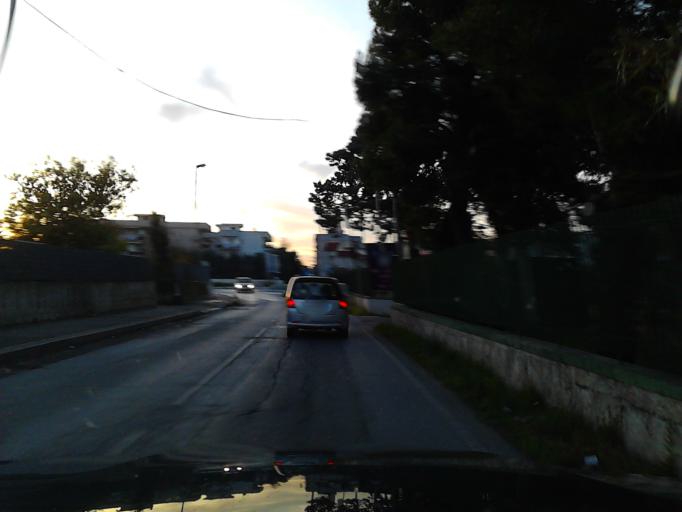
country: IT
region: Apulia
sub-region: Provincia di Bari
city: Valenzano
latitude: 41.0449
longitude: 16.8928
